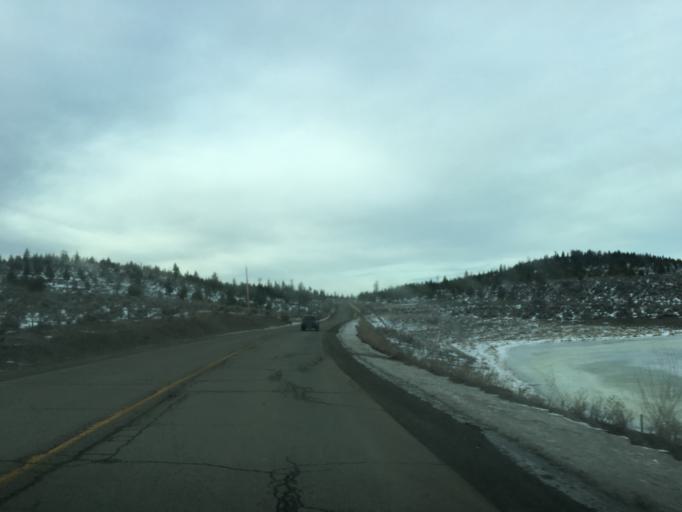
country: CA
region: British Columbia
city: Kamloops
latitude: 50.6309
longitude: -120.4437
